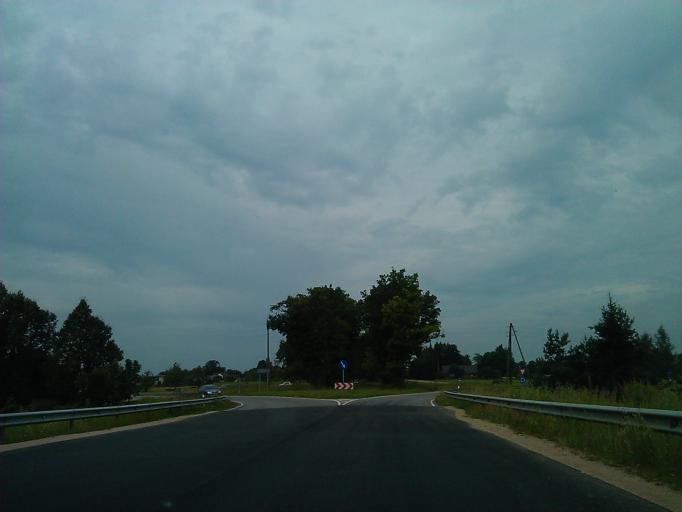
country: LV
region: Valmieras Rajons
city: Valmiera
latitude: 57.5108
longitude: 25.4232
